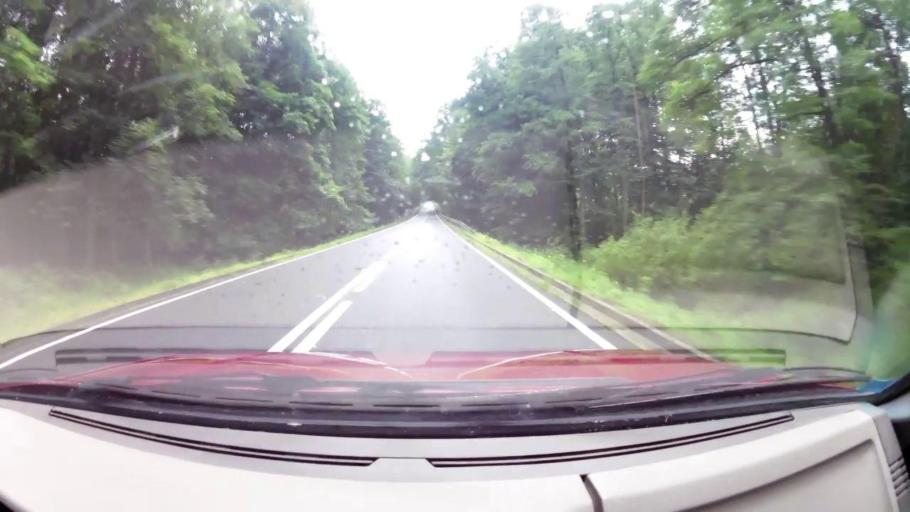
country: PL
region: West Pomeranian Voivodeship
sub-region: Powiat stargardzki
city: Chociwel
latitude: 53.4940
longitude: 15.4330
